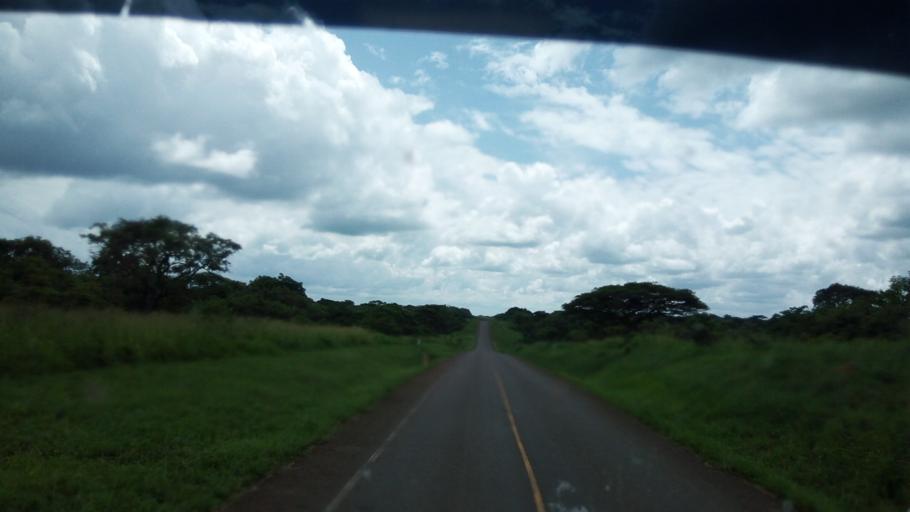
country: UG
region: Northern Region
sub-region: Oyam District
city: Oyam
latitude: 2.2964
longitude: 32.1957
